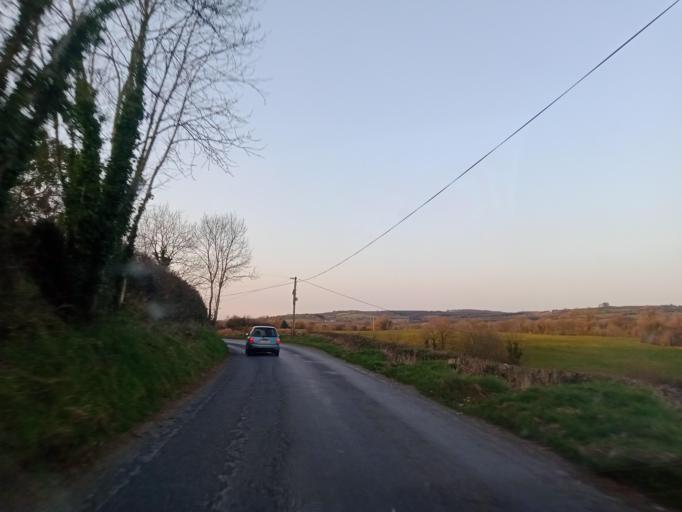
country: IE
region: Leinster
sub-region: Kilkenny
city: Castlecomer
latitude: 52.8541
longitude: -7.2635
